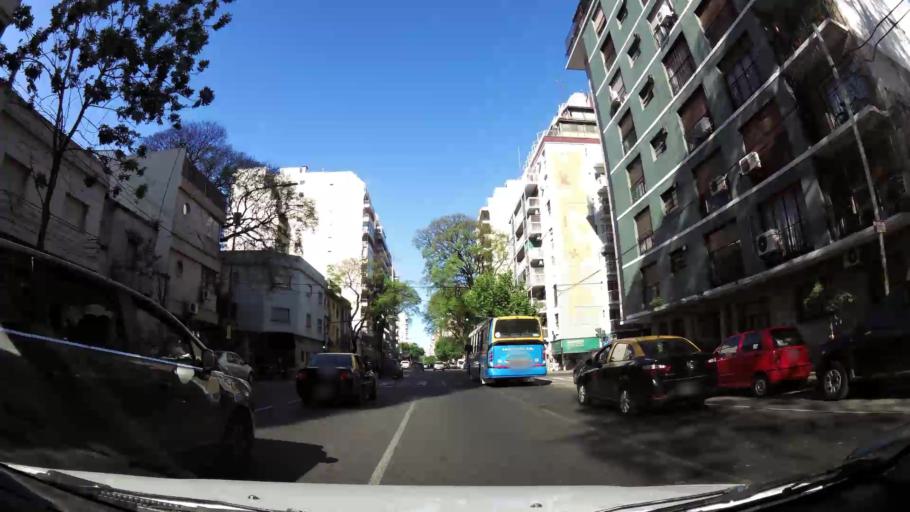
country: AR
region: Buenos Aires F.D.
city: Villa Santa Rita
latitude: -34.6248
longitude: -58.4664
